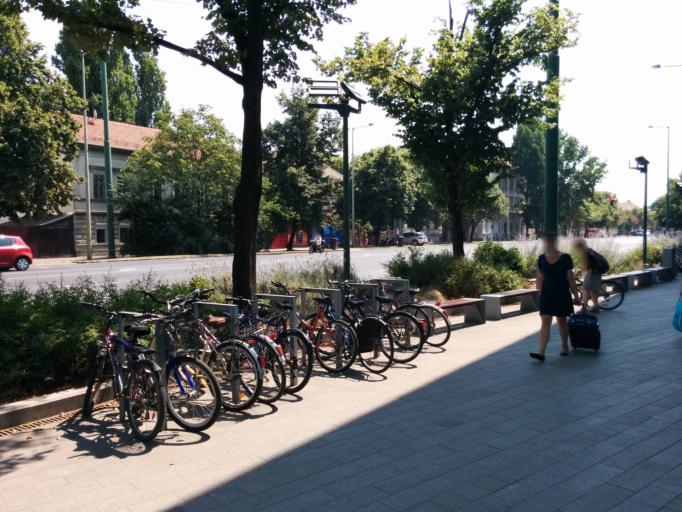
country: HU
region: Csongrad
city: Szeged
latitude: 46.2545
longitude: 20.1392
